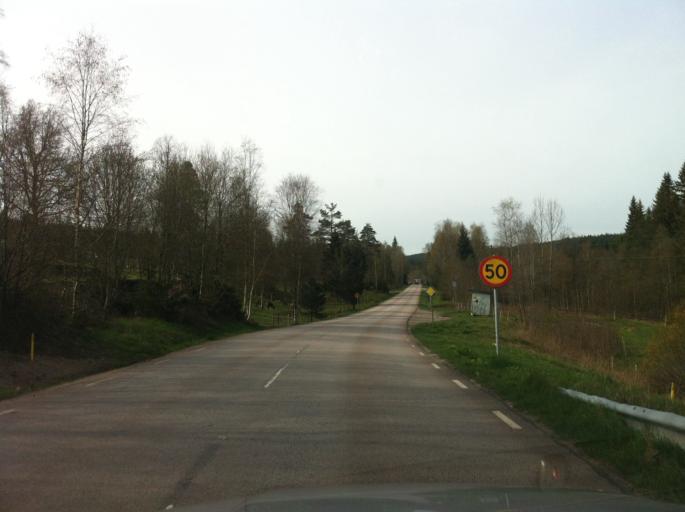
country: SE
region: Vaestra Goetaland
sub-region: Bollebygds Kommun
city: Bollebygd
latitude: 57.7276
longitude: 12.5901
